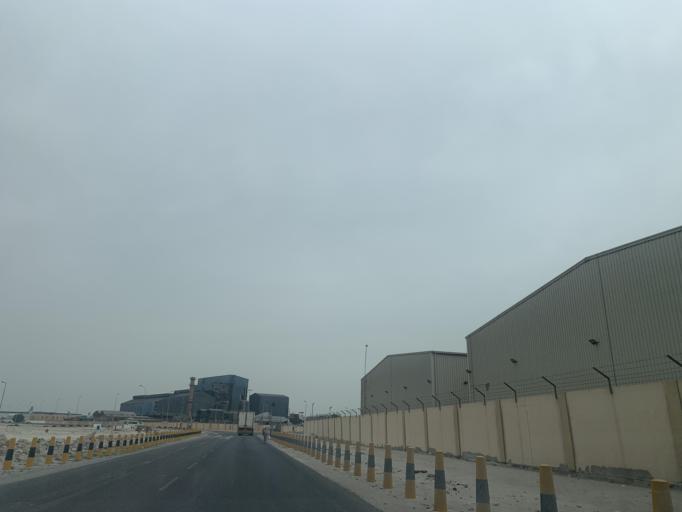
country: BH
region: Muharraq
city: Al Hadd
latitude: 26.2087
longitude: 50.6741
